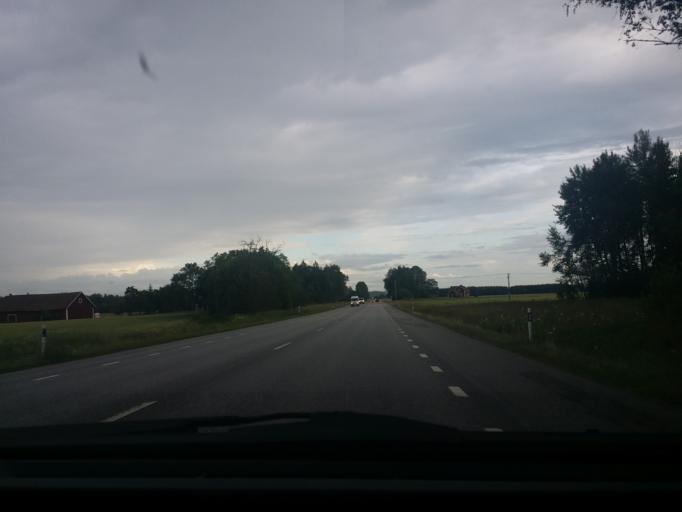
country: SE
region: OErebro
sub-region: Orebro Kommun
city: Hovsta
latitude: 59.4313
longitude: 15.1673
